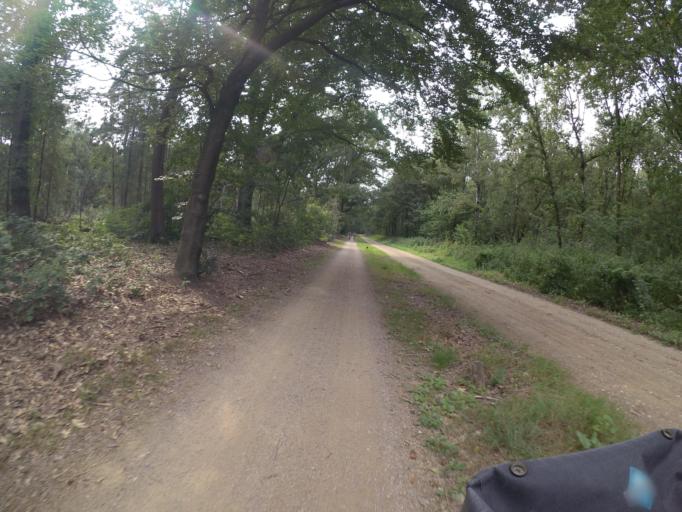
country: NL
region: Limburg
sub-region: Gemeente Gennep
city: Gennep
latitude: 51.6530
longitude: 6.0494
